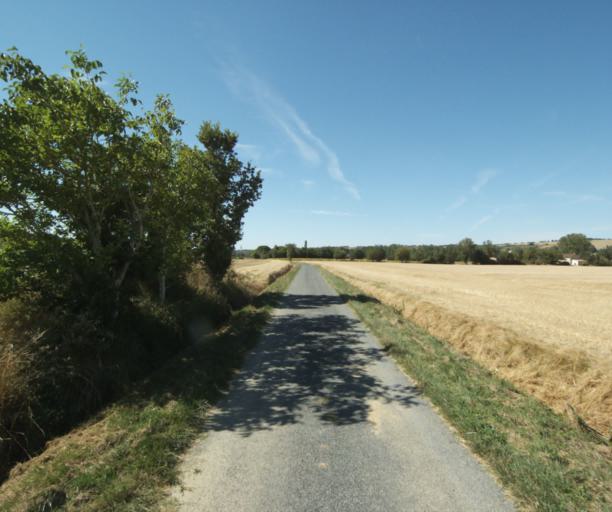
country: FR
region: Midi-Pyrenees
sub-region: Departement de la Haute-Garonne
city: Saint-Felix-Lauragais
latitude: 43.5032
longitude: 1.8947
